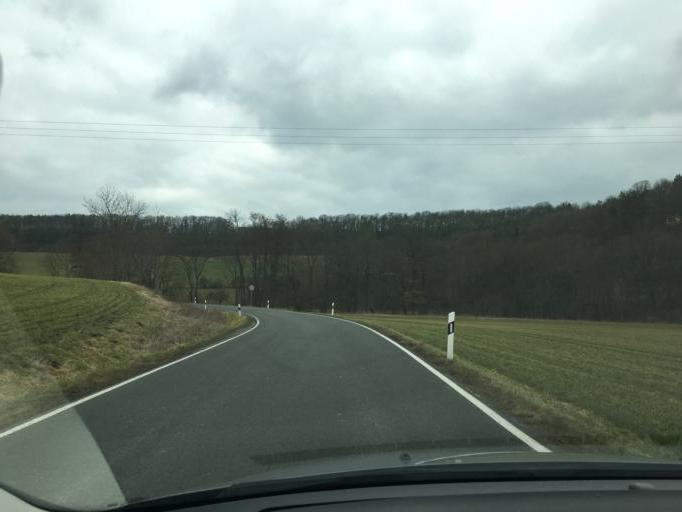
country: DE
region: Thuringia
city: Oettern
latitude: 50.9244
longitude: 11.3557
